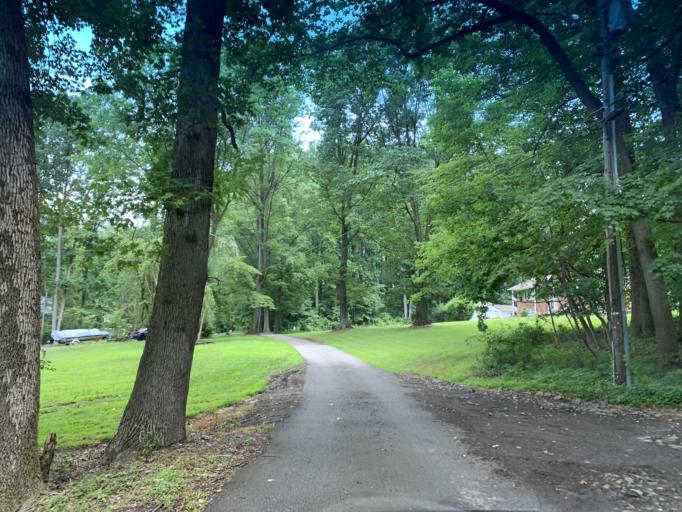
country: US
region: Maryland
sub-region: Baltimore County
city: Kingsville
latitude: 39.4461
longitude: -76.4507
